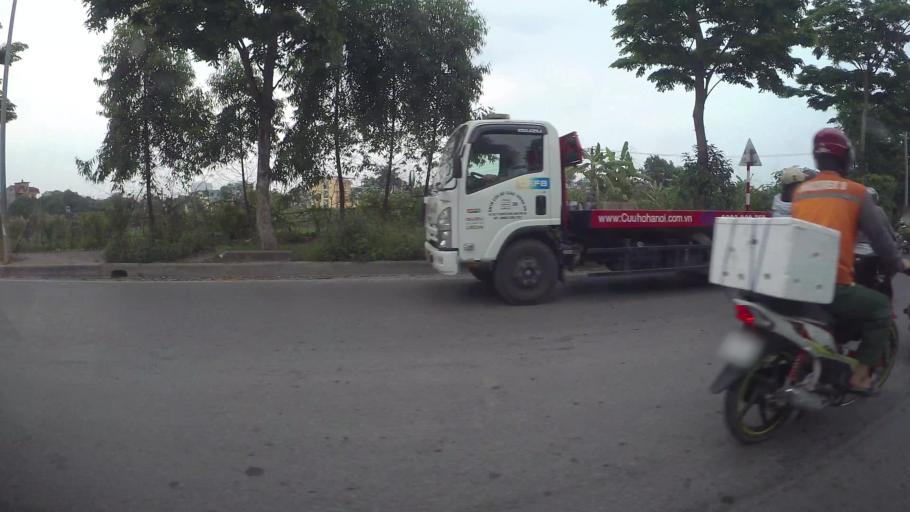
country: VN
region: Ha Noi
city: Trau Quy
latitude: 21.0074
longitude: 105.9132
